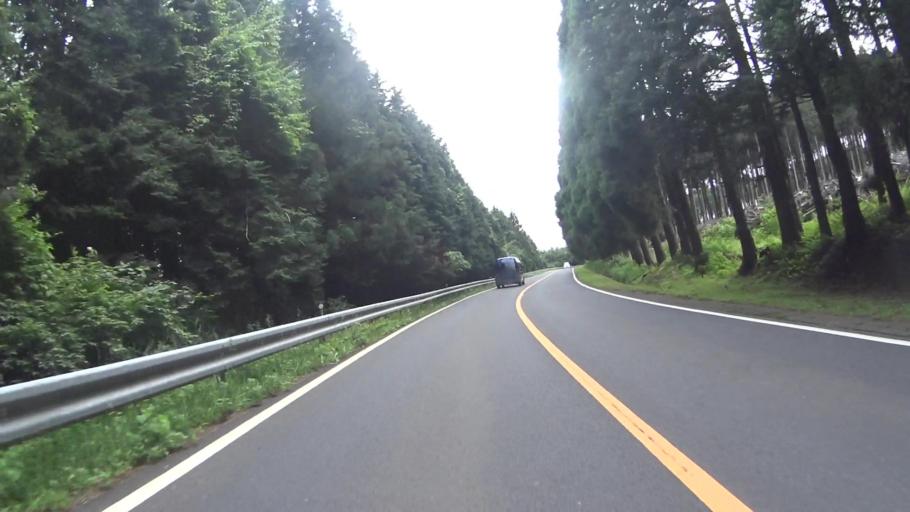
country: JP
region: Oita
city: Tsukawaki
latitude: 33.2119
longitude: 131.2978
